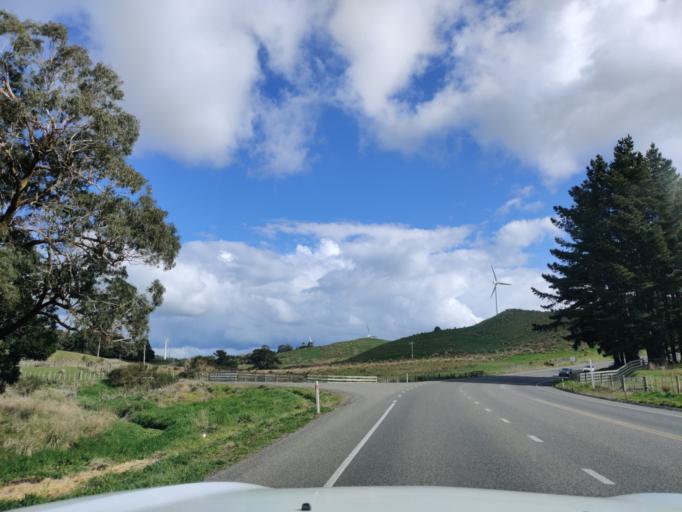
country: NZ
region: Manawatu-Wanganui
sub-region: Palmerston North City
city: Palmerston North
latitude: -40.2990
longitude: 175.8134
